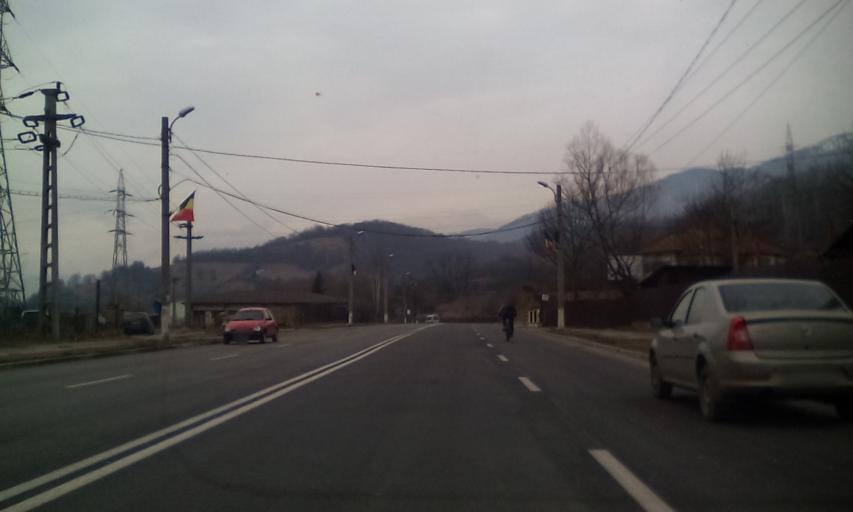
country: RO
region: Hunedoara
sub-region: Comuna Uricani
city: Uricani
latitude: 45.3444
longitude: 23.1824
